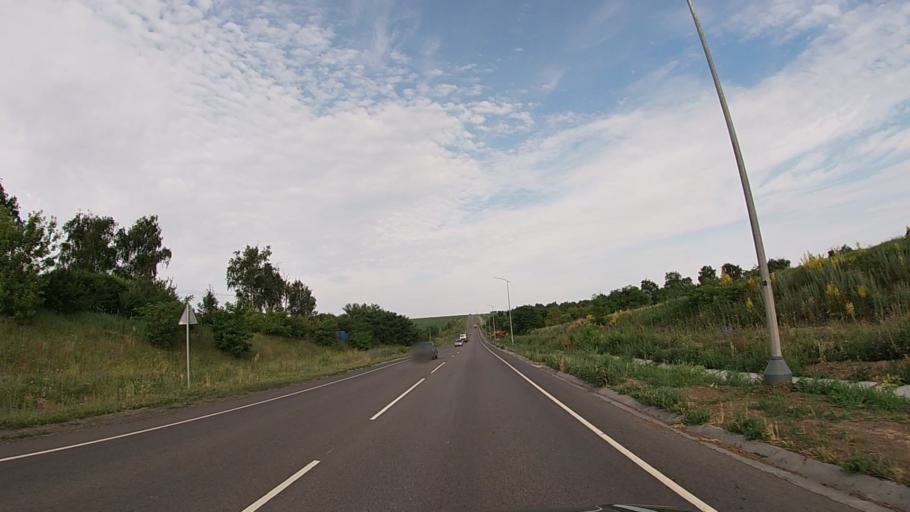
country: RU
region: Belgorod
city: Severnyy
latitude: 50.6643
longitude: 36.5236
